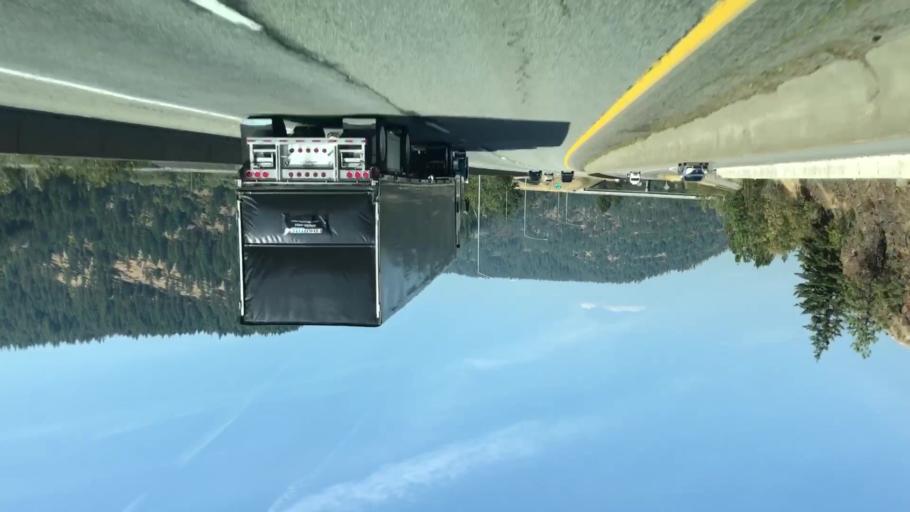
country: US
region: Idaho
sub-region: Kootenai County
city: Coeur d'Alene
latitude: 47.6233
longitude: -116.6546
